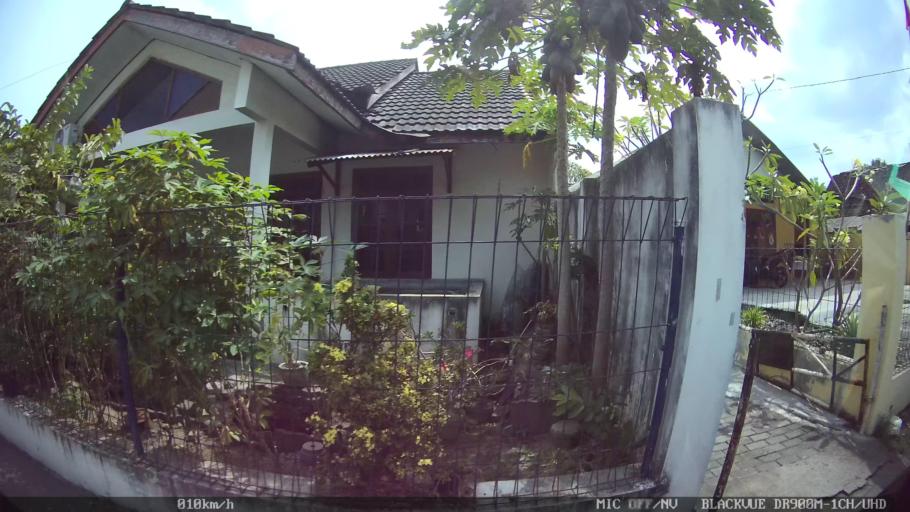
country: ID
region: Daerah Istimewa Yogyakarta
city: Depok
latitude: -7.7945
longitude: 110.4048
